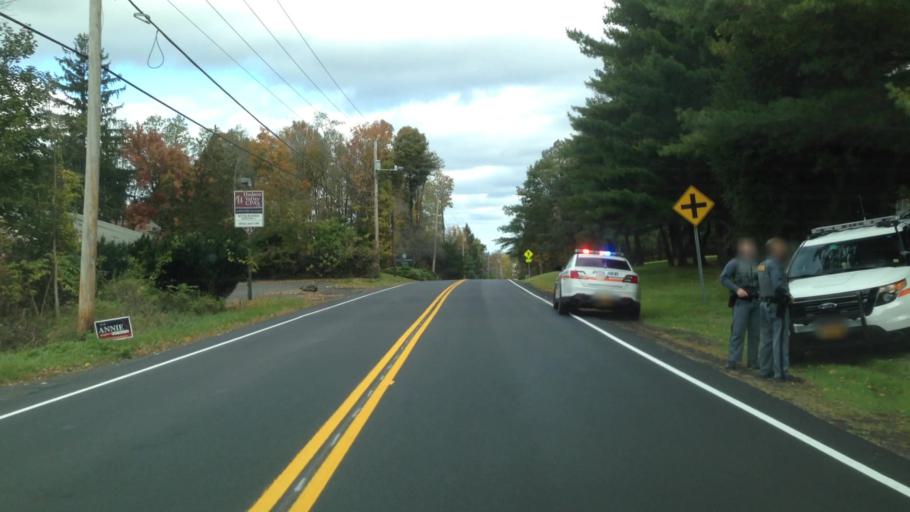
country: US
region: New York
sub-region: Ulster County
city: New Paltz
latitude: 41.7406
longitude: -74.0900
